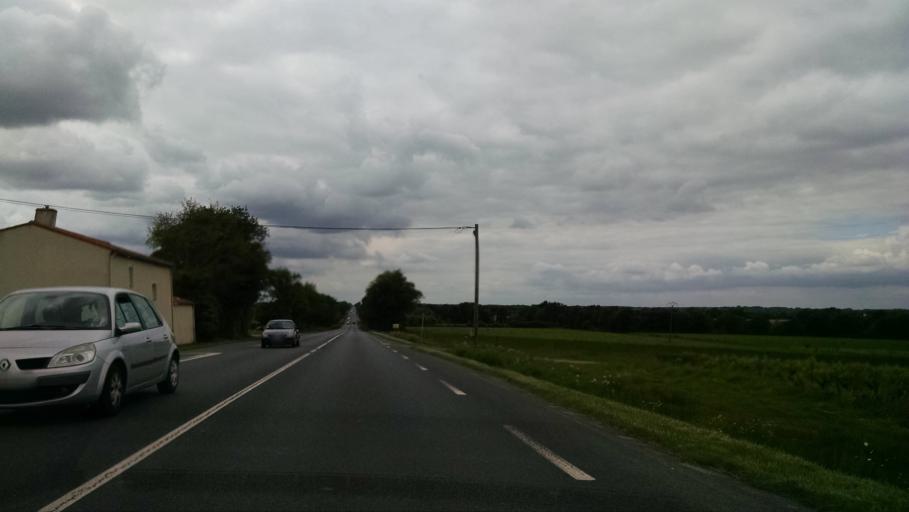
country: FR
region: Pays de la Loire
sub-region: Departement de la Loire-Atlantique
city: Aigrefeuille-sur-Maine
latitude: 47.0849
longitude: -1.4213
